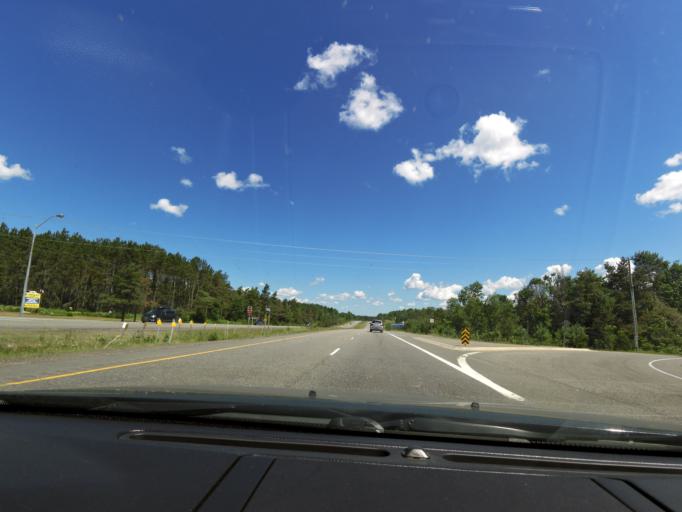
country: CA
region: Ontario
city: Bracebridge
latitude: 45.0726
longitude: -79.2968
